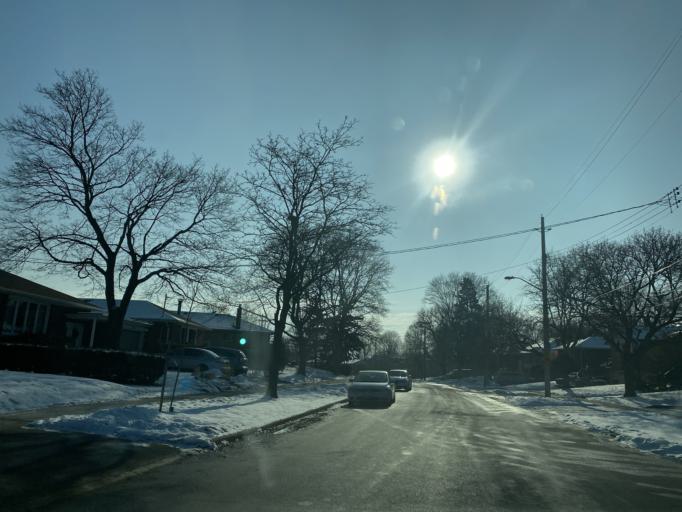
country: CA
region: Ontario
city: Etobicoke
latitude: 43.6679
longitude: -79.5646
